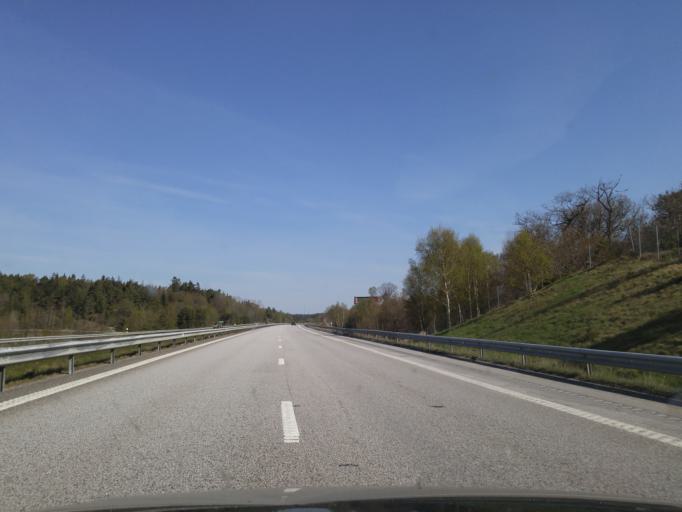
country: SE
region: Vaestra Goetaland
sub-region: Stenungsunds Kommun
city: Stenungsund
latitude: 58.0854
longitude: 11.8840
